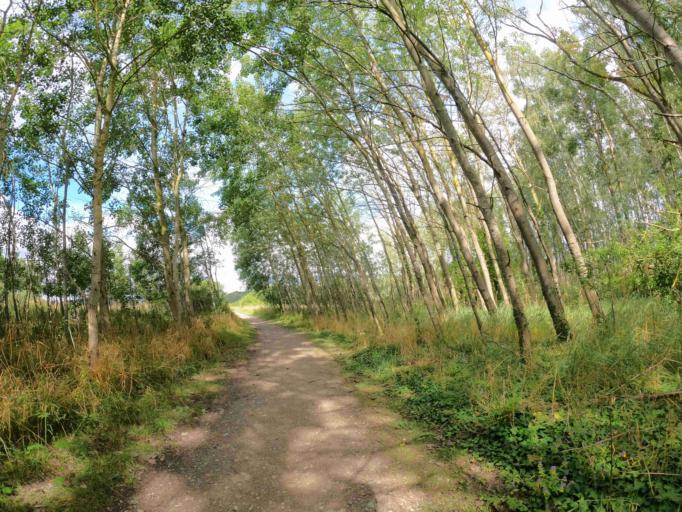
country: DE
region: Mecklenburg-Vorpommern
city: Putbus
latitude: 54.3420
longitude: 13.5354
